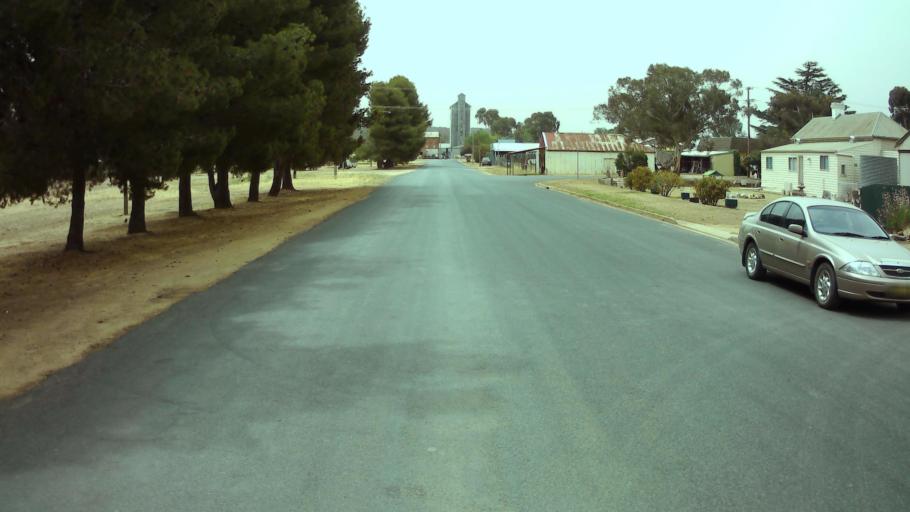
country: AU
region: New South Wales
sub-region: Weddin
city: Grenfell
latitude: -33.8974
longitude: 148.1558
